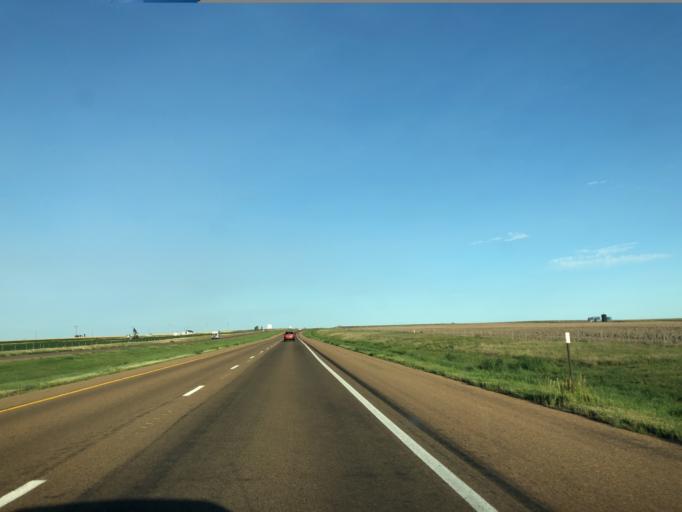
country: US
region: Kansas
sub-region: Russell County
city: Russell
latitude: 38.8639
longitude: -98.9394
